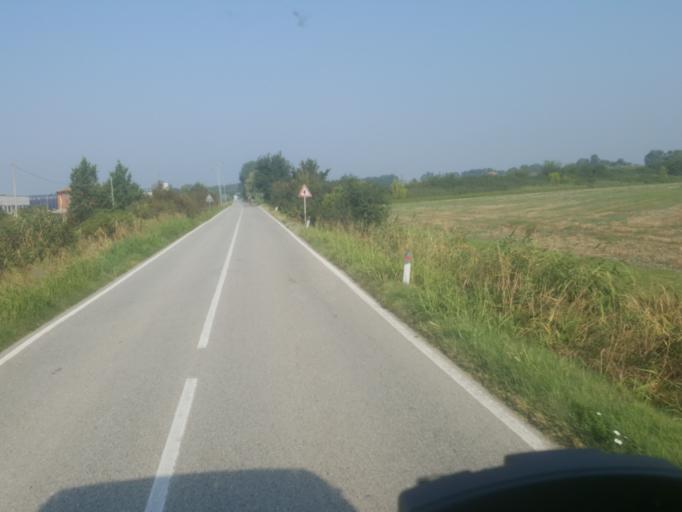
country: IT
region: Emilia-Romagna
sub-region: Provincia di Ravenna
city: Lavezzola
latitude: 44.5704
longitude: 11.8880
